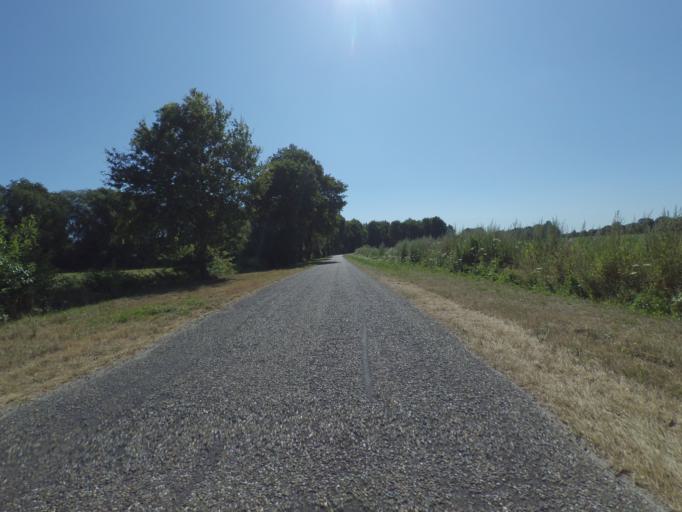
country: NL
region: Drenthe
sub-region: Gemeente Aa en Hunze
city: Anloo
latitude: 52.9721
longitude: 6.7022
